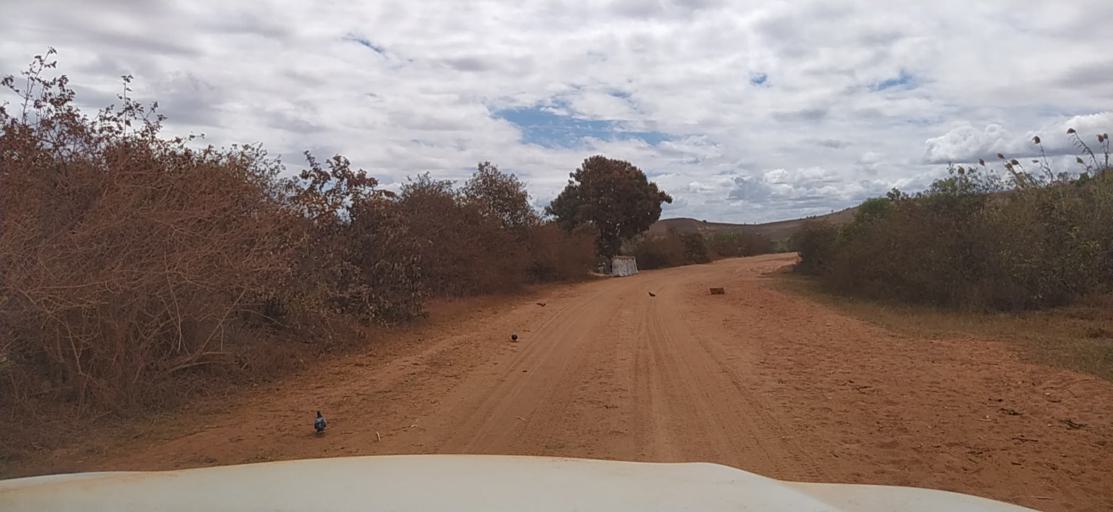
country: MG
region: Alaotra Mangoro
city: Ambatondrazaka
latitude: -18.0035
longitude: 48.2633
